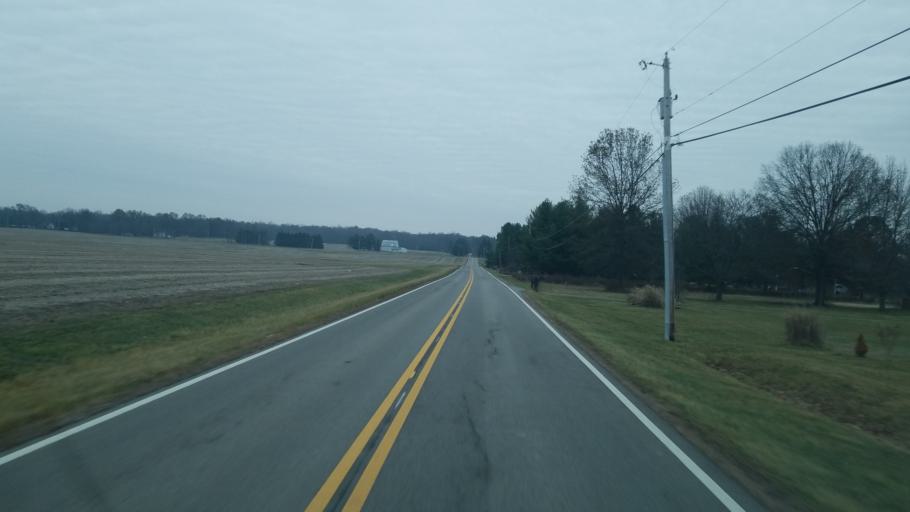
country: US
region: Ohio
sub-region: Delaware County
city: Sunbury
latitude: 40.3435
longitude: -82.8404
